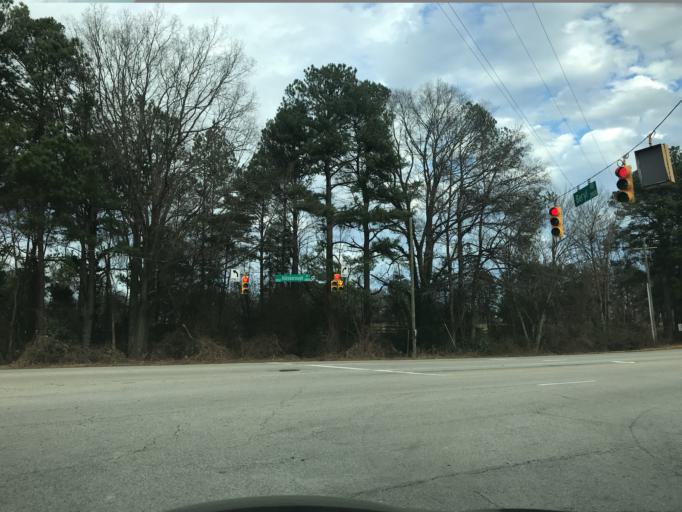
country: US
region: North Carolina
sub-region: Wake County
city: West Raleigh
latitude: 35.7947
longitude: -78.6911
